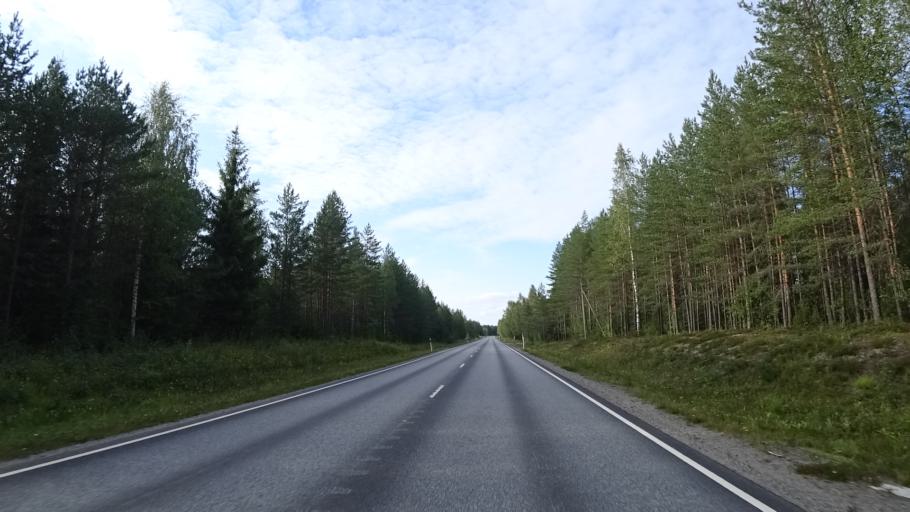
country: FI
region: North Karelia
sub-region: Joensuu
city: Eno
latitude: 62.8808
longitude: 30.2008
